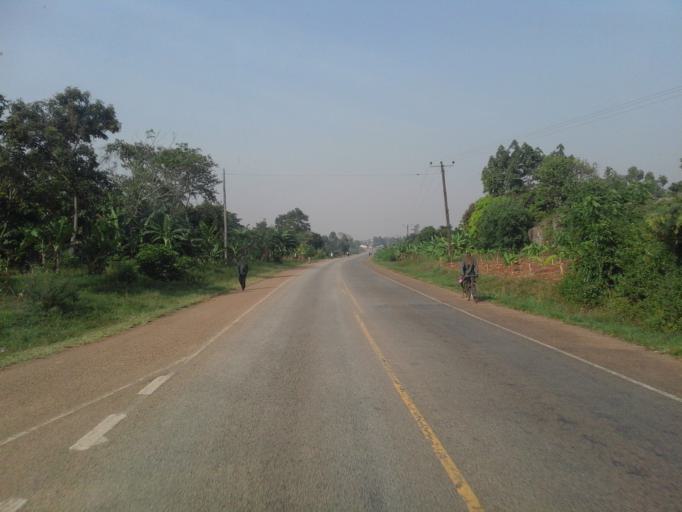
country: UG
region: Eastern Region
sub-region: Budaka District
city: Budaka
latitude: 1.0223
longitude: 33.9718
